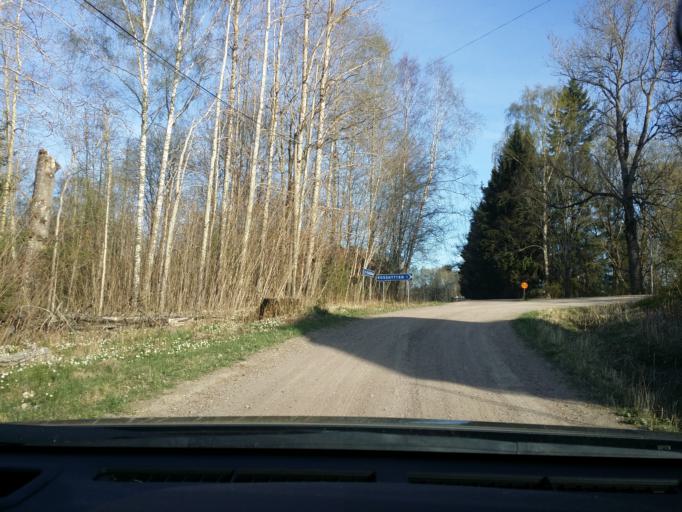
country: SE
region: Dalarna
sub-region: Avesta Kommun
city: Avesta
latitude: 60.0709
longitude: 16.3698
